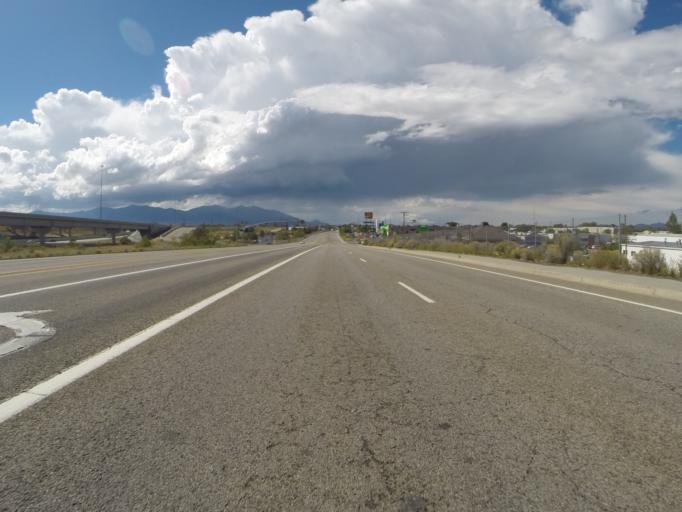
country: US
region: Utah
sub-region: Salt Lake County
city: South Salt Lake
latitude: 40.7256
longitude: -111.9099
